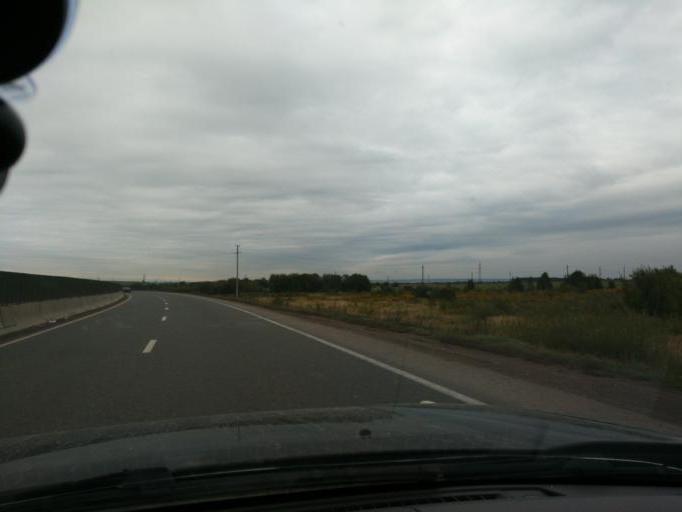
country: RU
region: Perm
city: Froly
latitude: 57.9283
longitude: 56.1854
